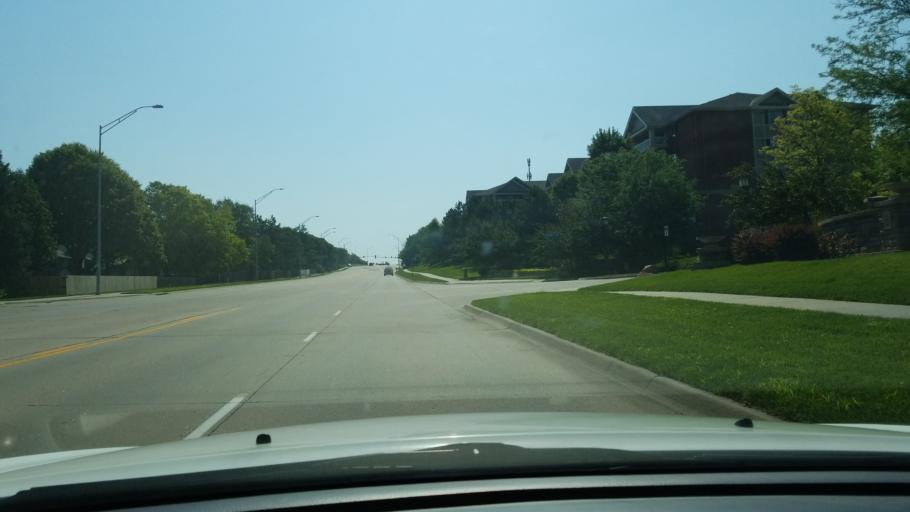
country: US
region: Nebraska
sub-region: Lancaster County
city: Lincoln
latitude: 40.7696
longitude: -96.6117
